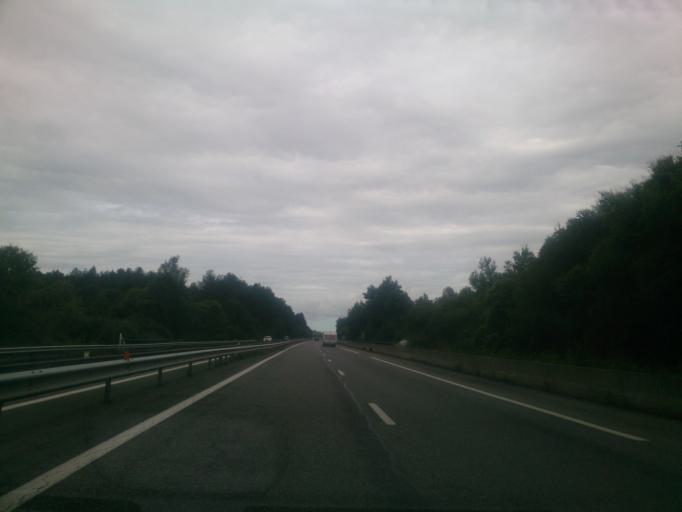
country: FR
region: Midi-Pyrenees
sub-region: Departement des Hautes-Pyrenees
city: Lannemezan
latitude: 43.1043
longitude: 0.4735
